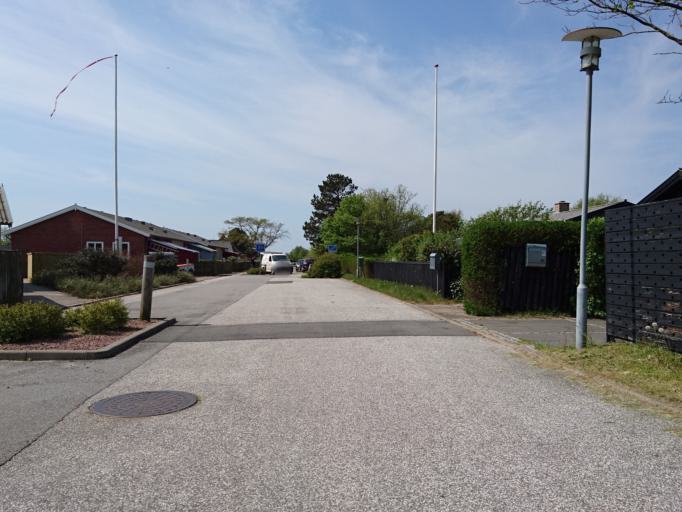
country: DK
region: North Denmark
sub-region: Frederikshavn Kommune
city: Skagen
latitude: 57.7248
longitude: 10.5753
